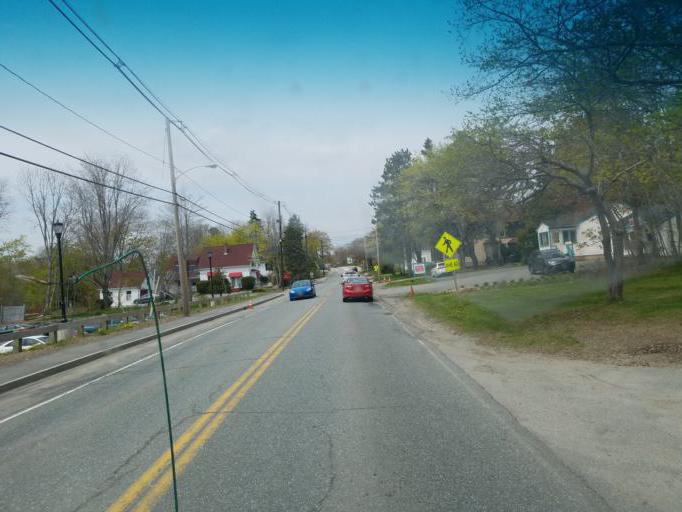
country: US
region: Maine
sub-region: Hancock County
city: Ellsworth
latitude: 44.5475
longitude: -68.4237
